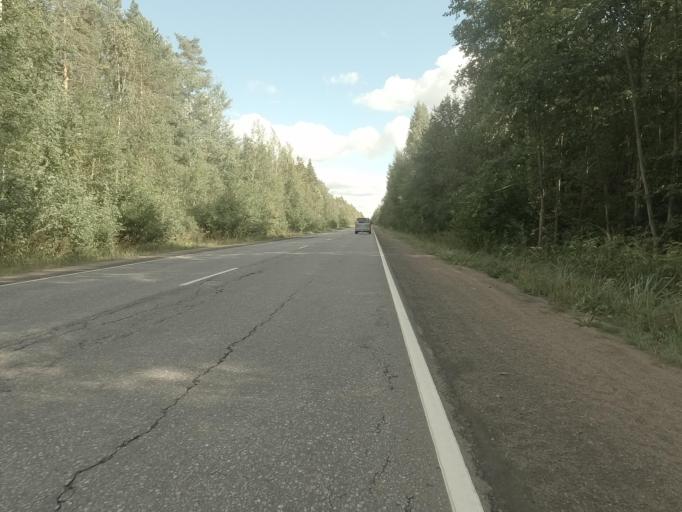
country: RU
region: Leningrad
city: Shcheglovo
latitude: 60.0025
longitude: 30.8683
